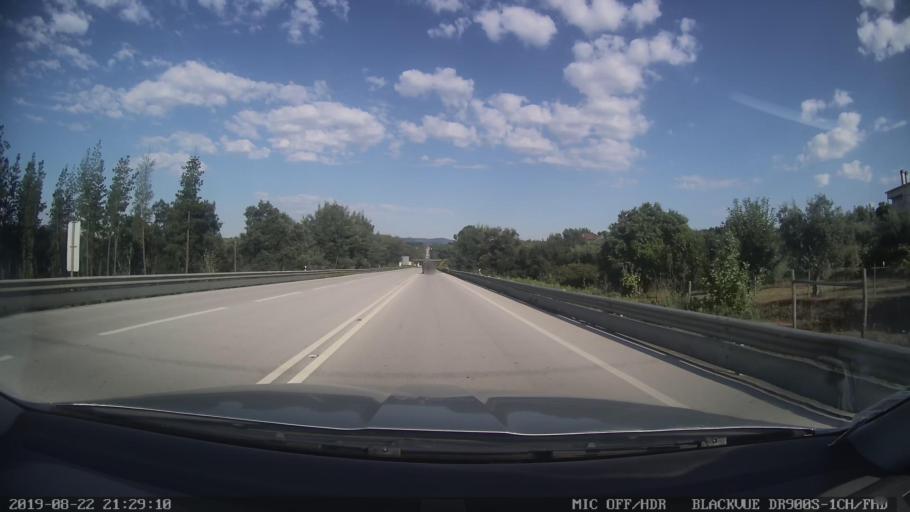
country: PT
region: Leiria
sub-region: Pedrogao Grande
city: Pedrogao Grande
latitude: 39.9003
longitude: -8.1310
